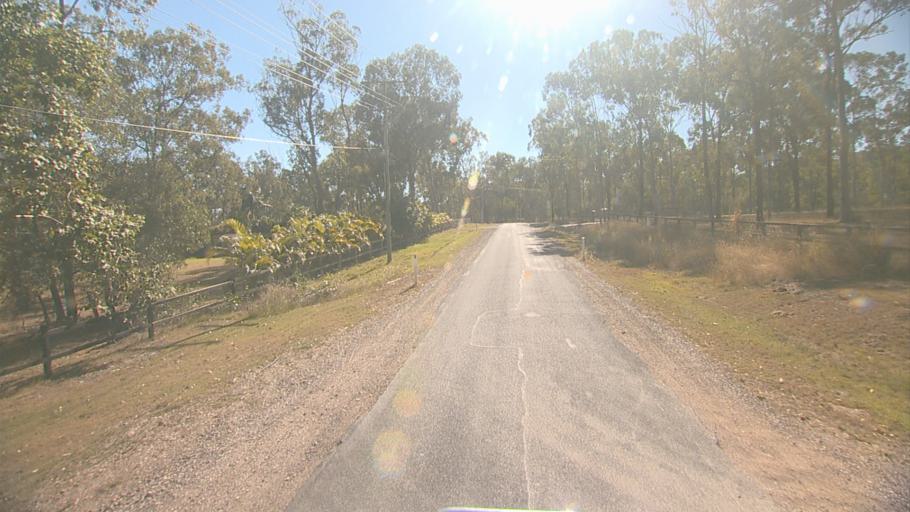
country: AU
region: Queensland
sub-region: Logan
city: Chambers Flat
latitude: -27.7721
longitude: 153.1419
